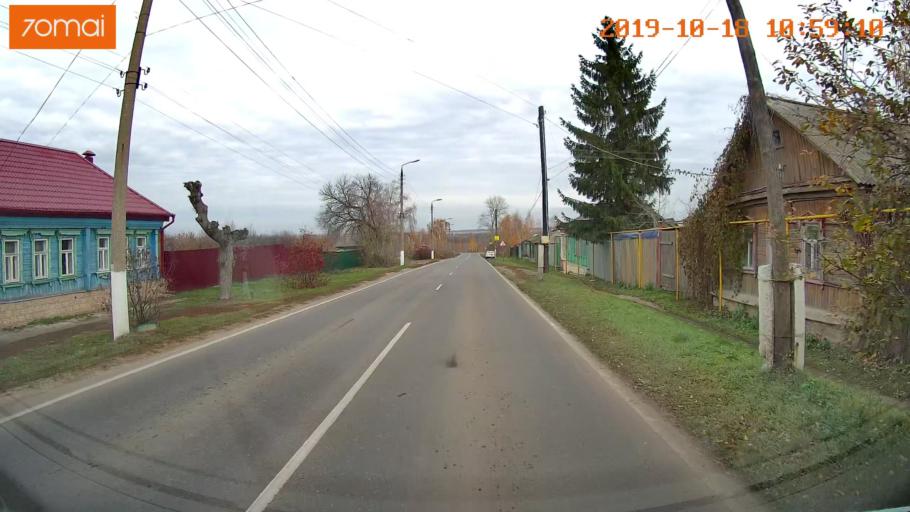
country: RU
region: Tula
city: Yepifan'
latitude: 53.8276
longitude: 38.5551
